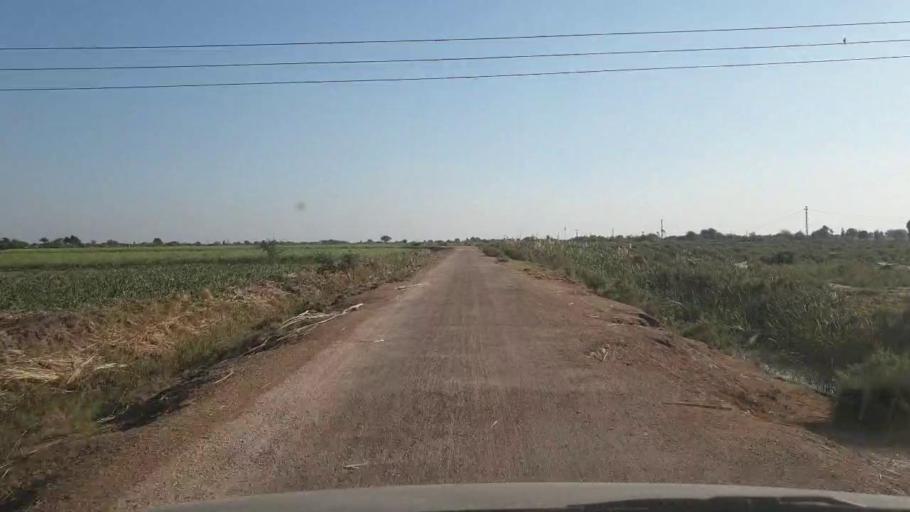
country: PK
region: Sindh
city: Mirwah Gorchani
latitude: 25.3719
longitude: 69.0960
